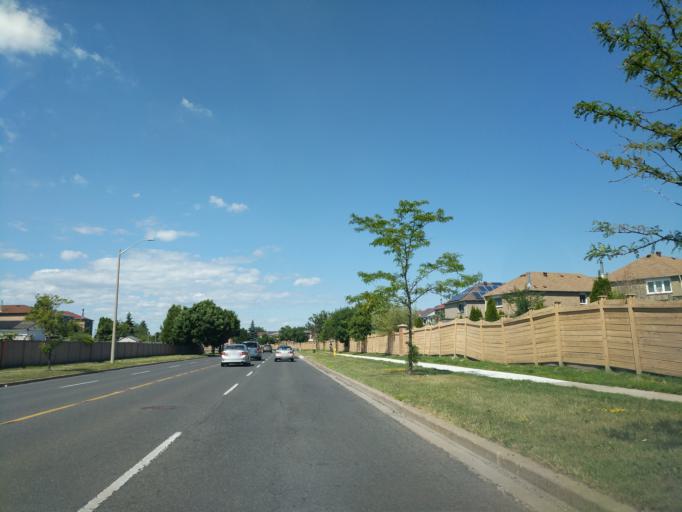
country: CA
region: Ontario
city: Markham
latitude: 43.8382
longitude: -79.2658
